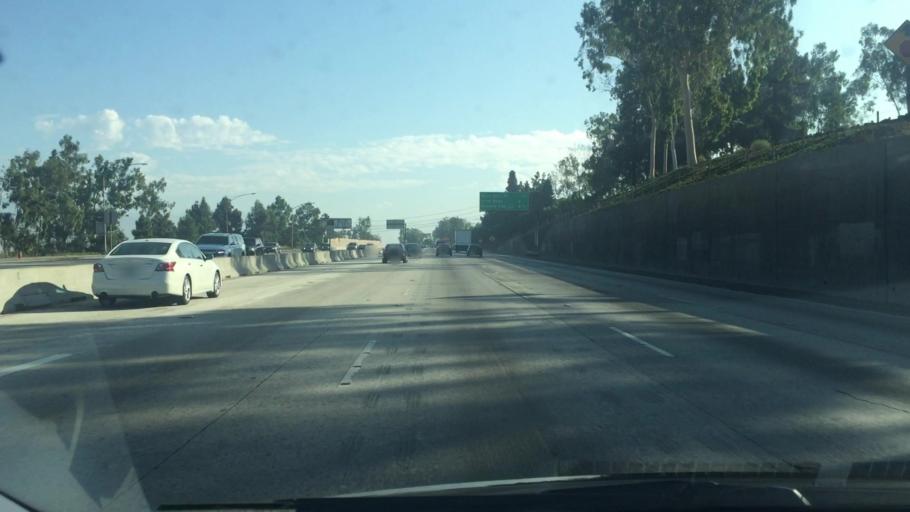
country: US
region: California
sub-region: Los Angeles County
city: West Whittier-Los Nietos
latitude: 34.0047
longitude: -118.0633
